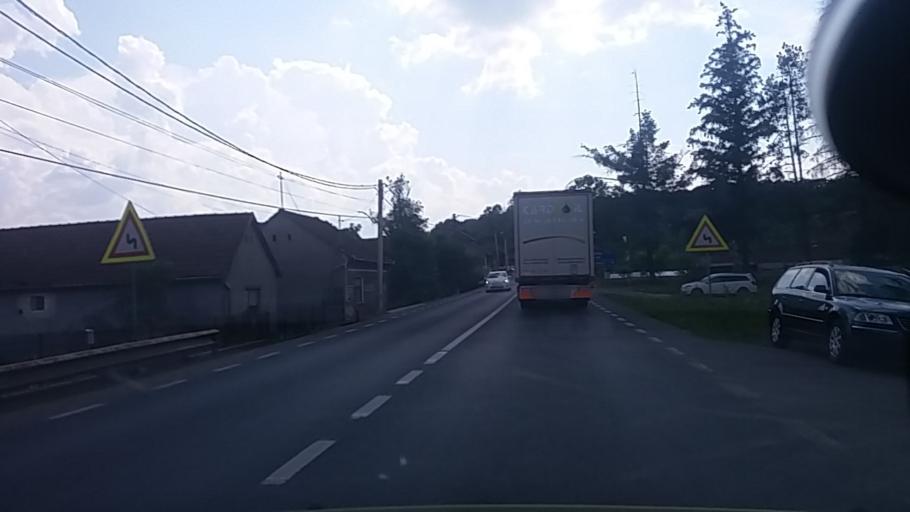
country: RO
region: Arad
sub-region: Comuna Savarsin
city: Savarsin
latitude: 46.0113
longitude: 22.2227
